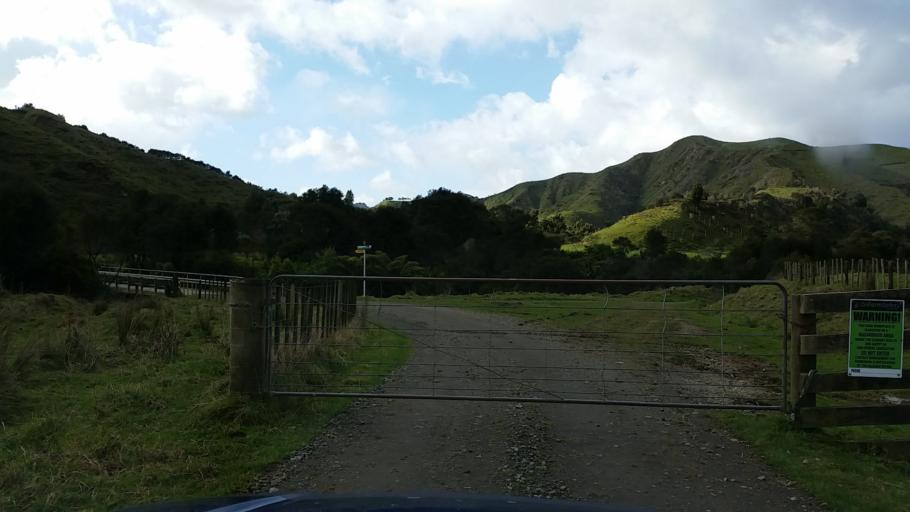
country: NZ
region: Taranaki
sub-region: South Taranaki District
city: Eltham
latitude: -39.2500
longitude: 174.8028
